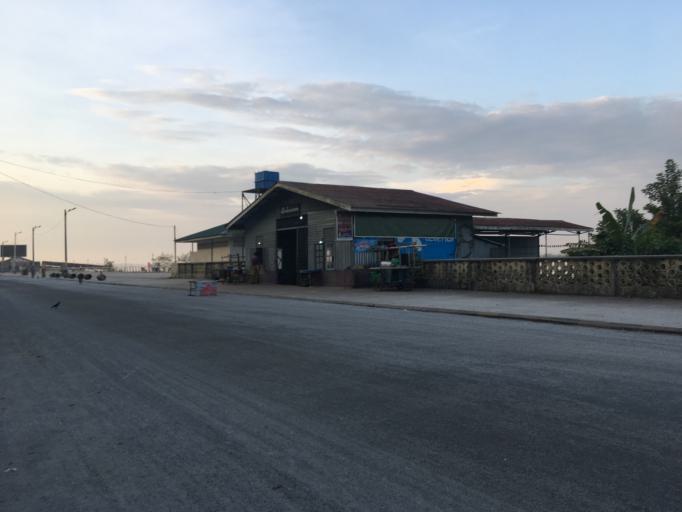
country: MM
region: Mon
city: Mawlamyine
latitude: 16.4834
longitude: 97.6186
